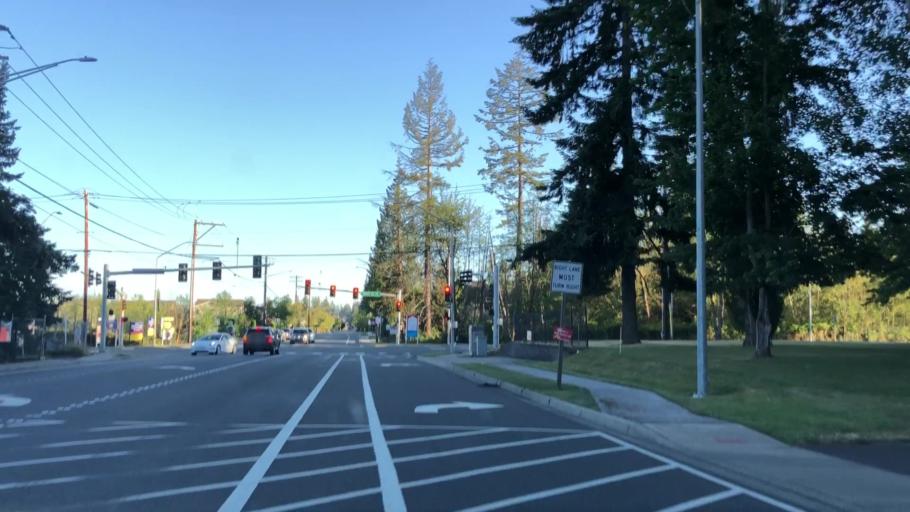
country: US
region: Washington
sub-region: Snohomish County
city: North Creek
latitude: 47.8352
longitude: -122.1858
